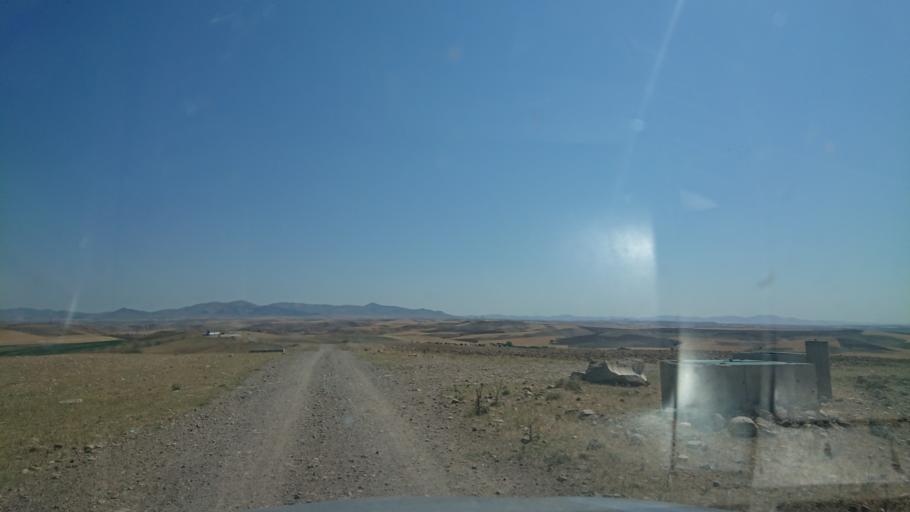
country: TR
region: Aksaray
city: Sariyahsi
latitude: 39.0547
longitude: 33.8868
